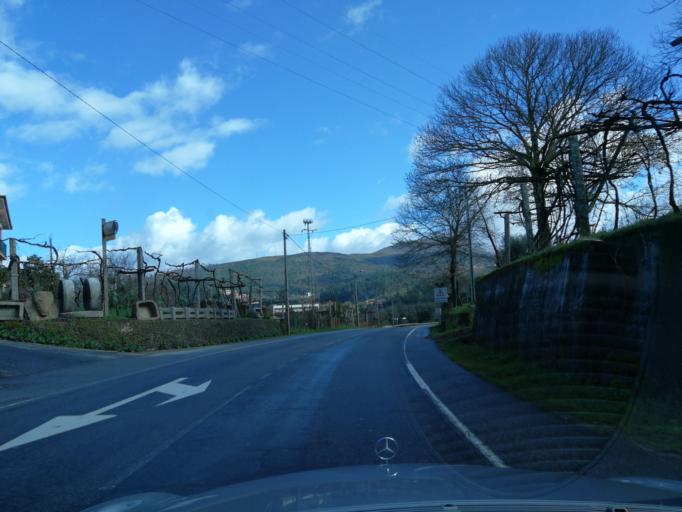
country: PT
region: Viana do Castelo
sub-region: Ponte da Barca
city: Ponte da Barca
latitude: 41.8077
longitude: -8.3696
